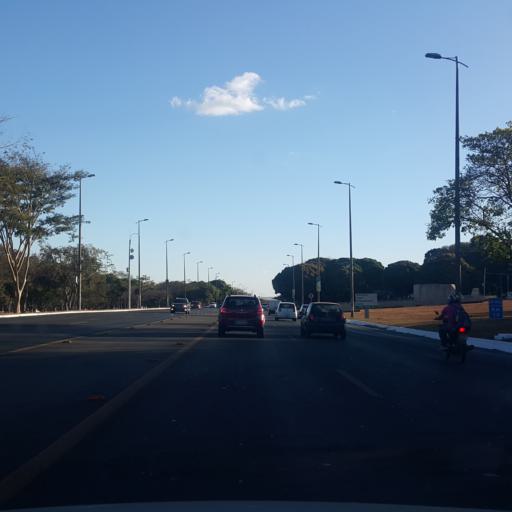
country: BR
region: Federal District
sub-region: Brasilia
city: Brasilia
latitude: -15.8143
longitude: -47.8973
